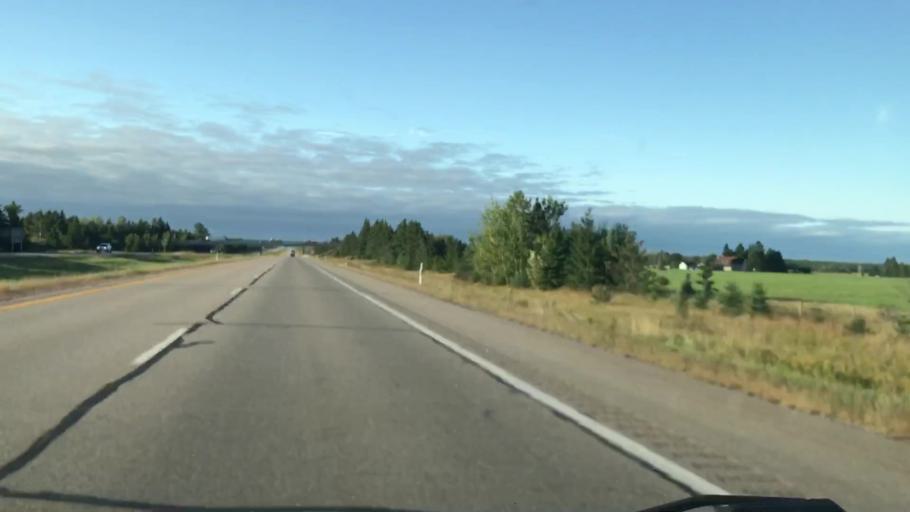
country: US
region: Michigan
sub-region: Chippewa County
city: Sault Ste. Marie
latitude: 46.4234
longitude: -84.3937
